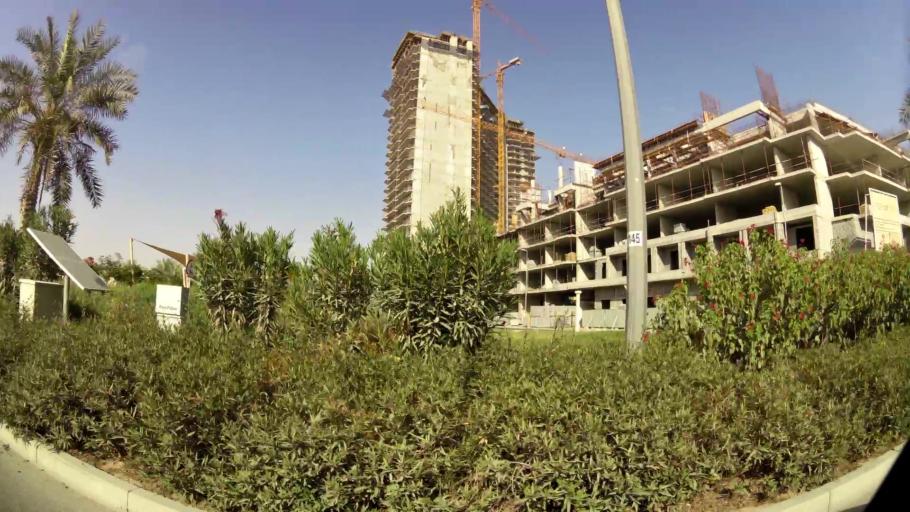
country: AE
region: Dubai
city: Dubai
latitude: 25.0568
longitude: 55.2031
